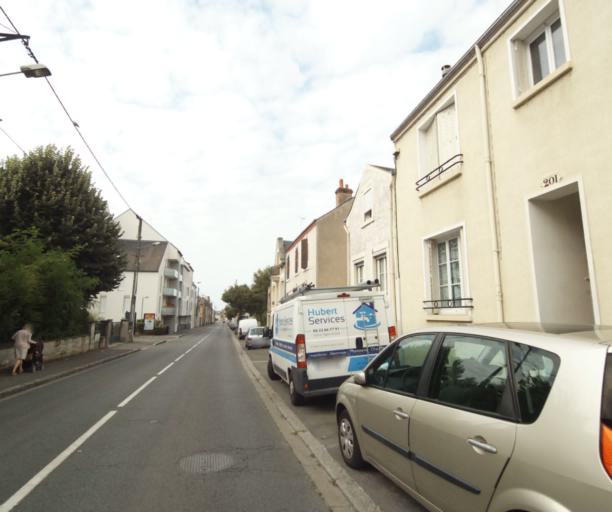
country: FR
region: Centre
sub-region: Departement du Loiret
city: Orleans
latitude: 47.9150
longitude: 1.9167
